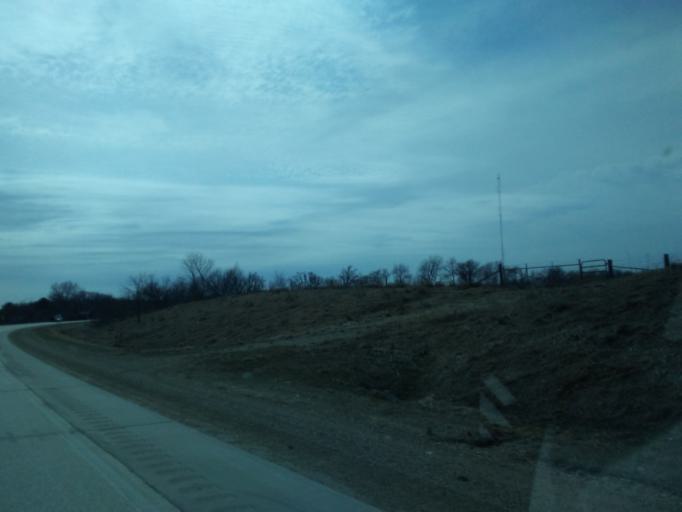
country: US
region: Iowa
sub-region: Winneshiek County
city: Decorah
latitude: 43.3474
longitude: -91.8059
